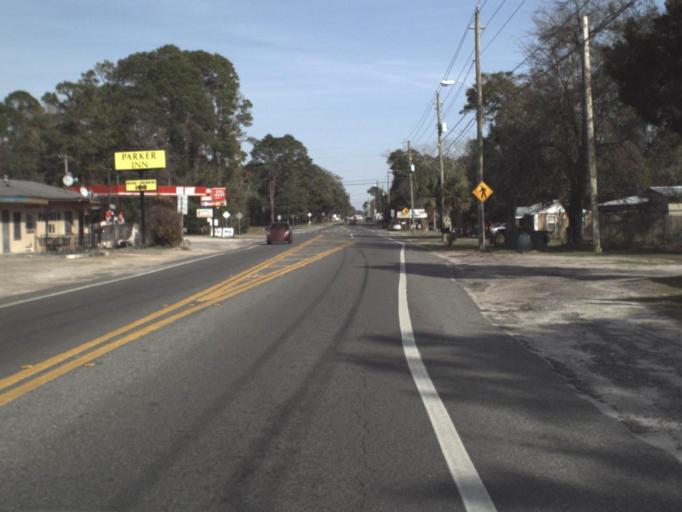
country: US
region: Florida
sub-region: Bay County
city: Parker
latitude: 30.1311
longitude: -85.6009
